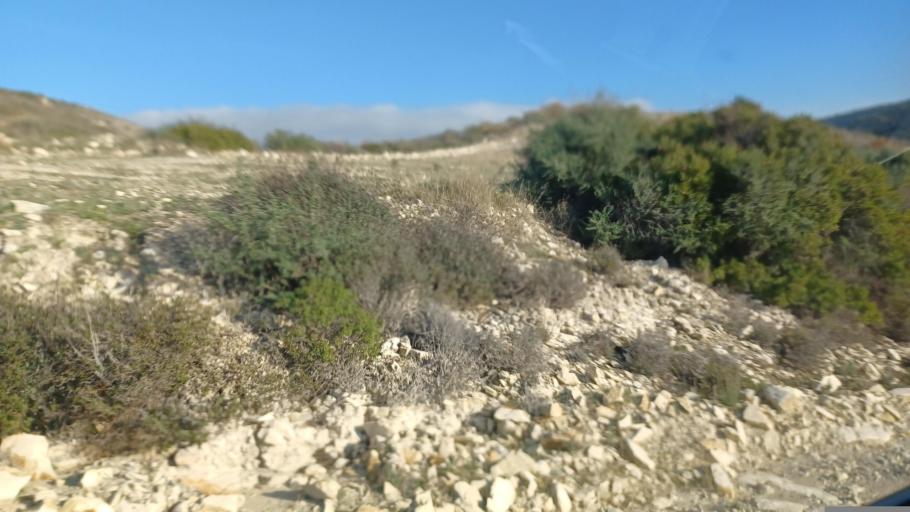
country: CY
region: Larnaka
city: Kofinou
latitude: 34.8309
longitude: 33.3037
